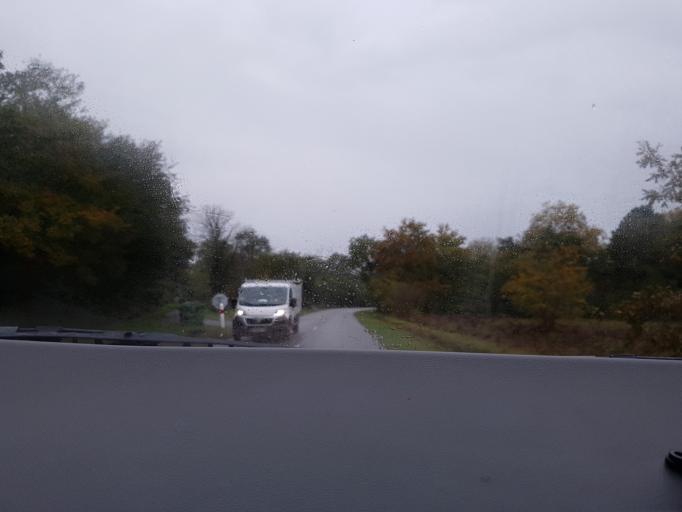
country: FR
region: Aquitaine
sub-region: Departement de la Gironde
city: Saint-Symphorien
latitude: 44.2653
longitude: -0.5554
